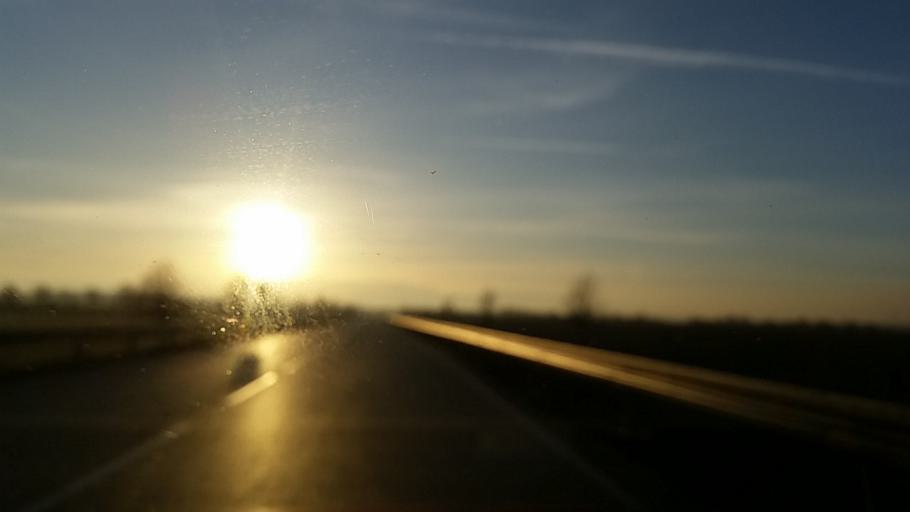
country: DE
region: Saxony-Anhalt
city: Frose
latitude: 51.7658
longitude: 11.4083
